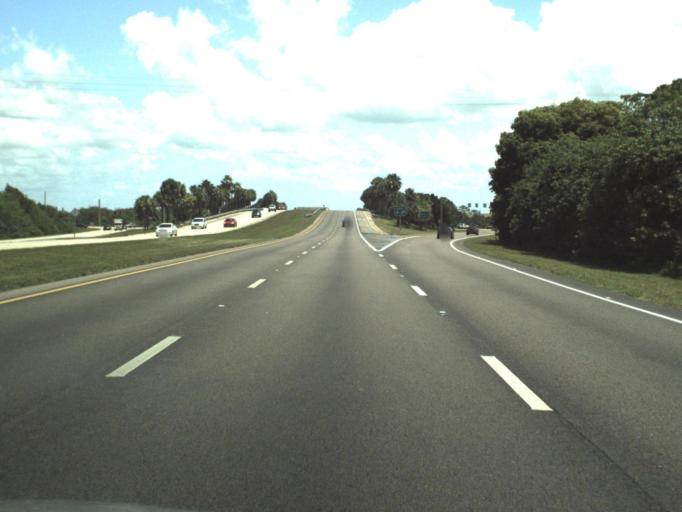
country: US
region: Florida
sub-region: Brevard County
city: Cocoa
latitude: 28.4052
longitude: -80.7093
